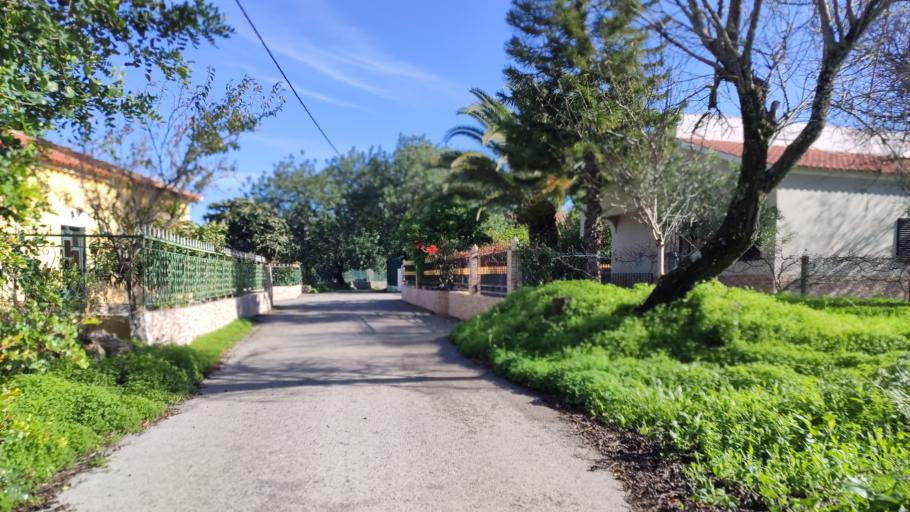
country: PT
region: Faro
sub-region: Sao Bras de Alportel
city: Sao Bras de Alportel
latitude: 37.1502
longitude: -7.8732
